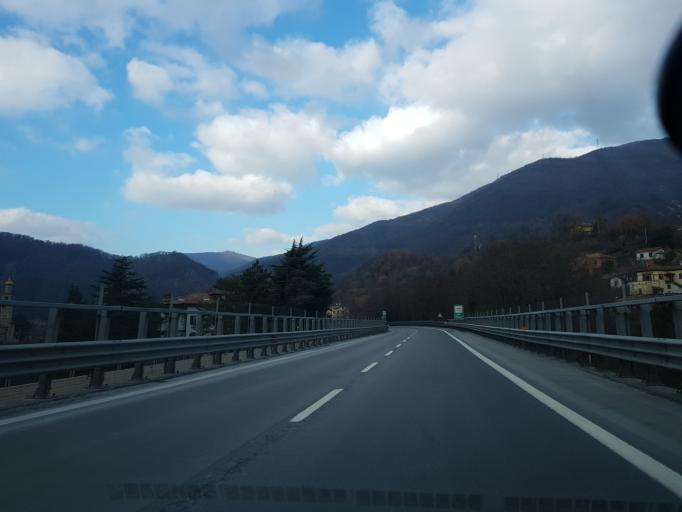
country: IT
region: Liguria
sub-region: Provincia di Genova
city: Isola del Cantone
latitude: 44.6449
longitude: 8.9593
